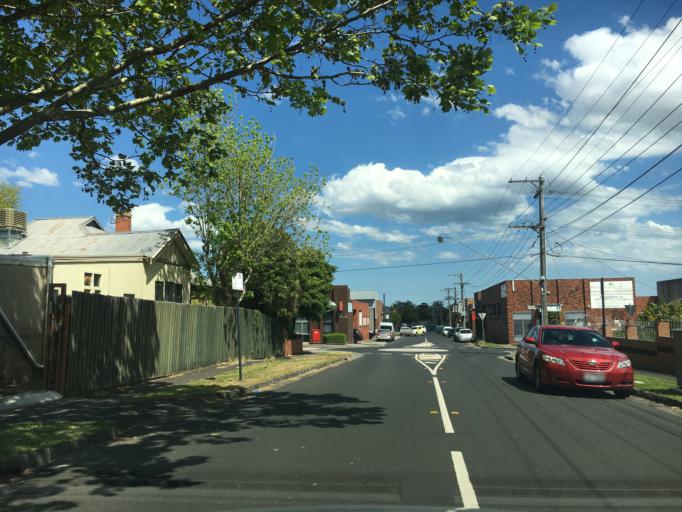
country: AU
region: Victoria
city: Hughesdale
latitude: -37.9019
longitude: 145.0955
